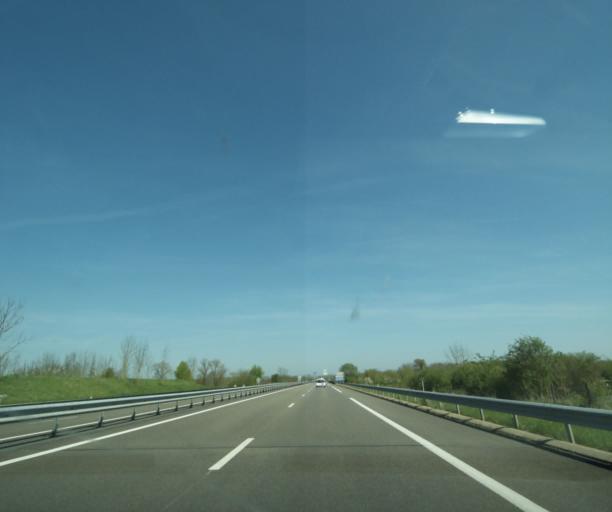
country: FR
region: Bourgogne
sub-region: Departement de la Nievre
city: Sermoise-sur-Loire
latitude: 46.9507
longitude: 3.1679
